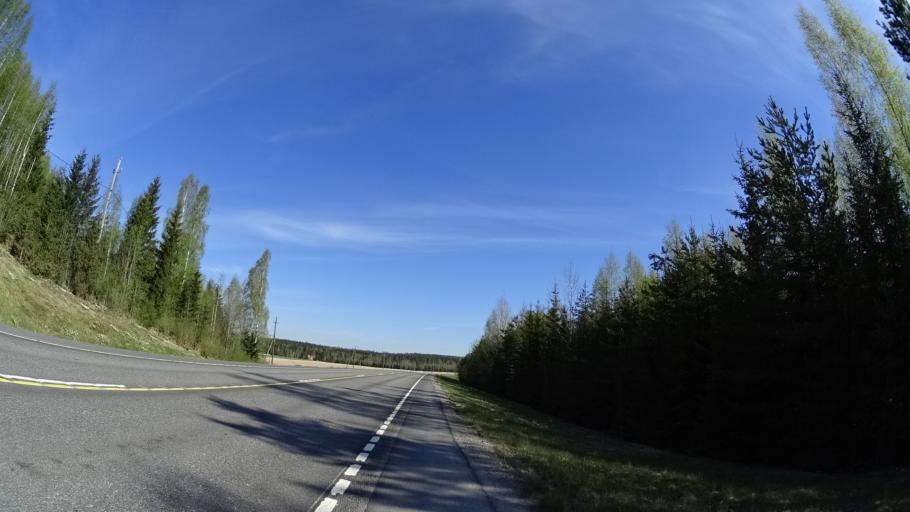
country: FI
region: Uusimaa
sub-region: Helsinki
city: Nurmijaervi
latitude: 60.4187
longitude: 24.8238
